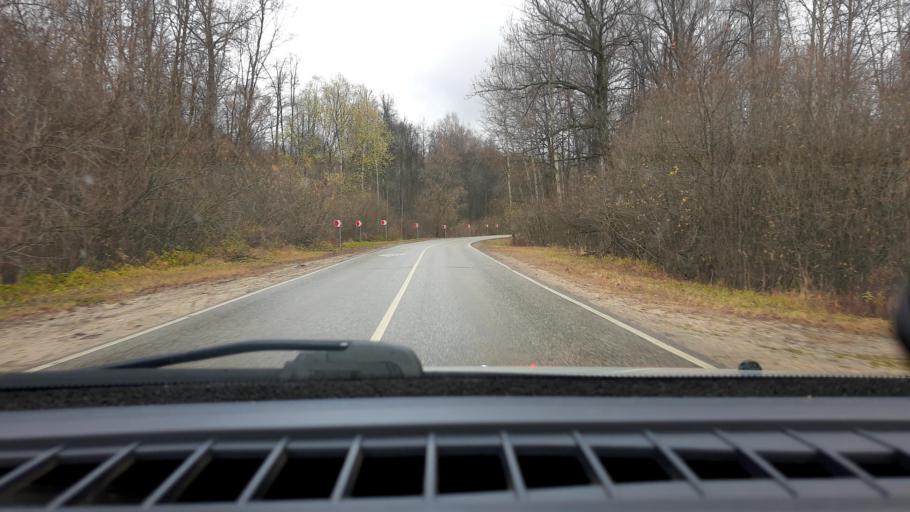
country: RU
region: Nizjnij Novgorod
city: Afonino
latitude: 56.1868
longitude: 44.0236
